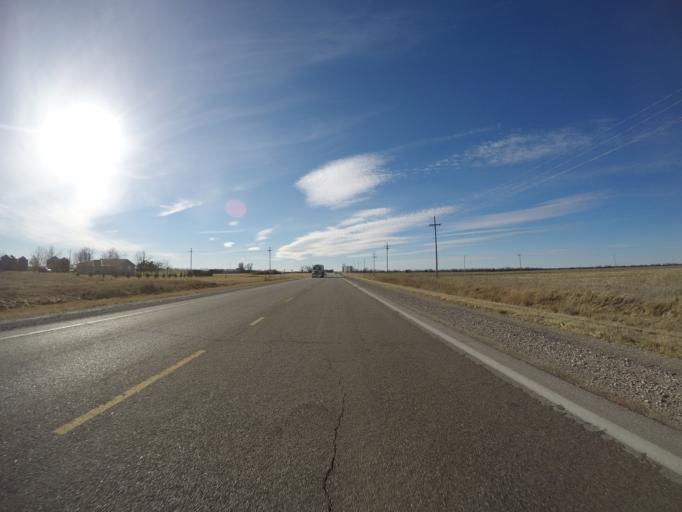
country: US
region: Kansas
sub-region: McPherson County
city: Moundridge
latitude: 38.3768
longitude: -97.4440
